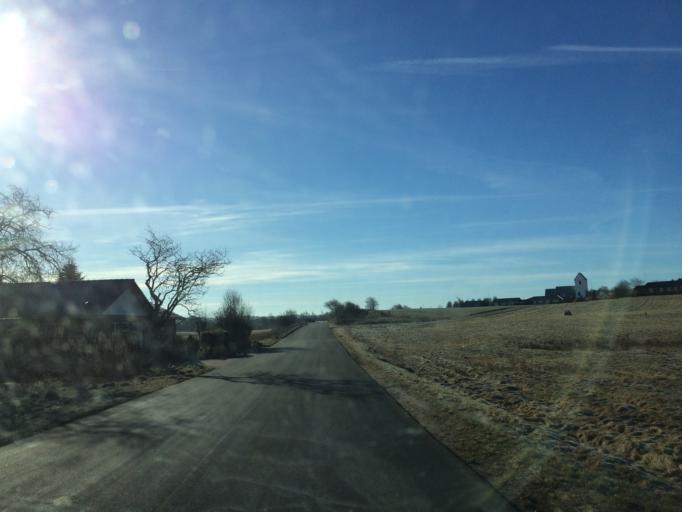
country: DK
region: North Denmark
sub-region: Mariagerfjord Kommune
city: Hobro
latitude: 56.5946
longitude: 9.6327
